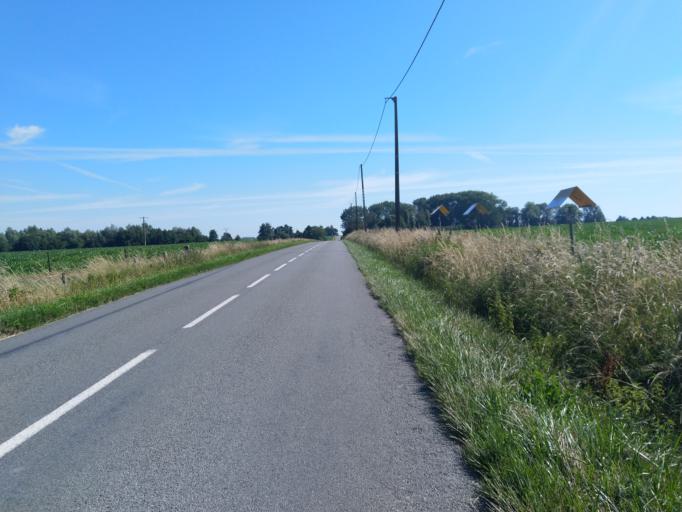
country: FR
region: Nord-Pas-de-Calais
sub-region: Departement du Nord
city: Bavay
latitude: 50.3099
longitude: 3.8063
